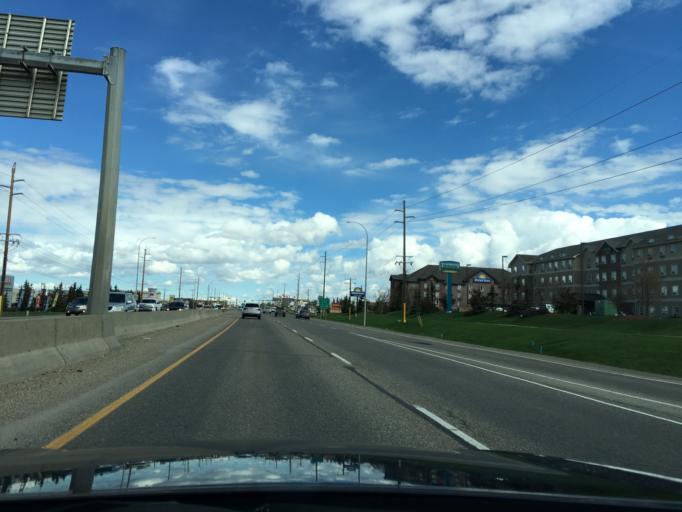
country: CA
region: Alberta
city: Calgary
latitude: 51.0705
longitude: -114.0016
